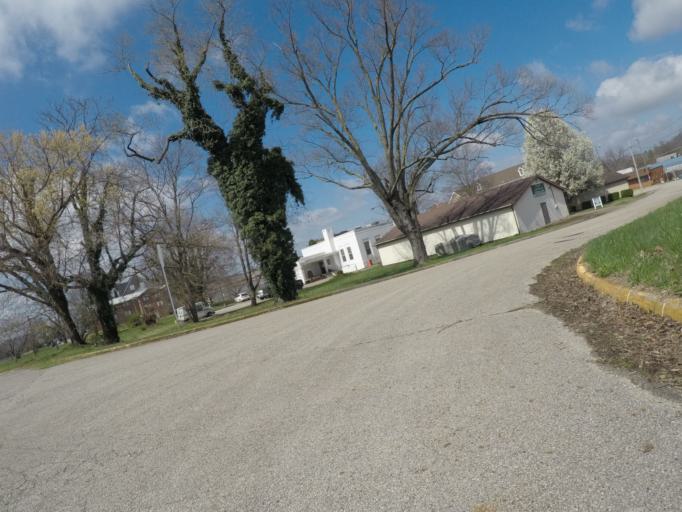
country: US
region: West Virginia
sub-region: Wayne County
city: Kenova
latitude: 38.3983
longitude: -82.5771
